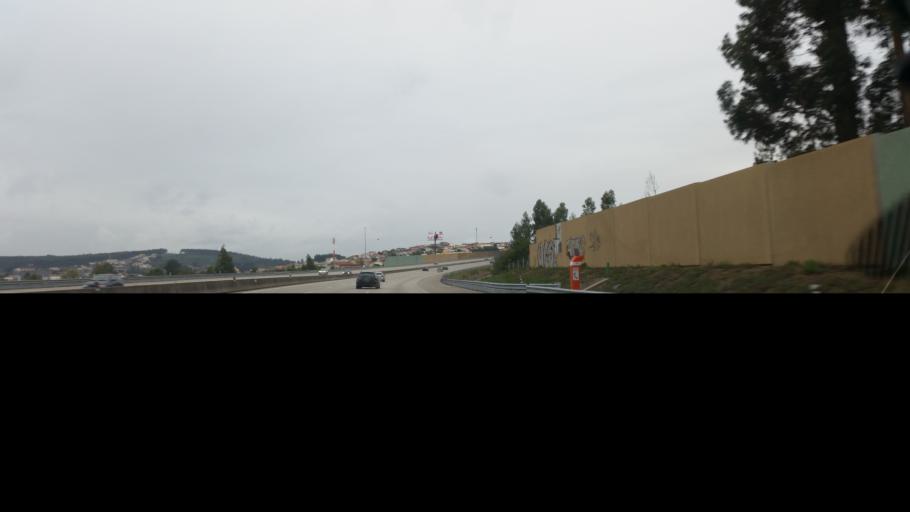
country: PT
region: Porto
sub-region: Trofa
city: Sao Romao do Coronado
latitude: 41.2759
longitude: -8.5604
